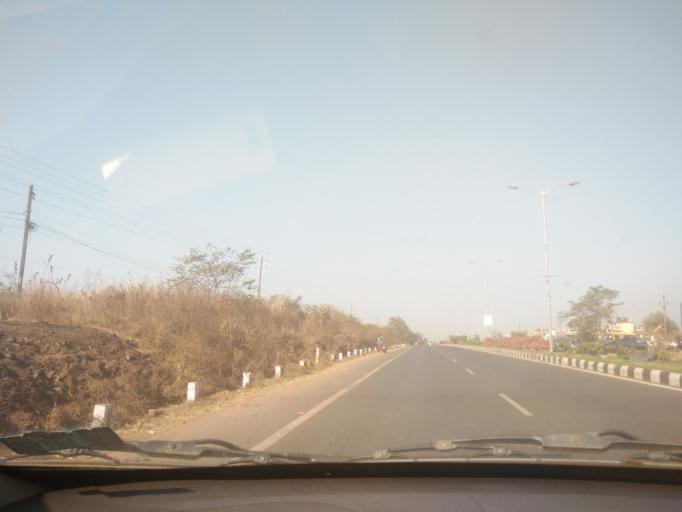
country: IN
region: Goa
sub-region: South Goa
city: Chicalim
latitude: 15.3874
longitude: 73.8631
